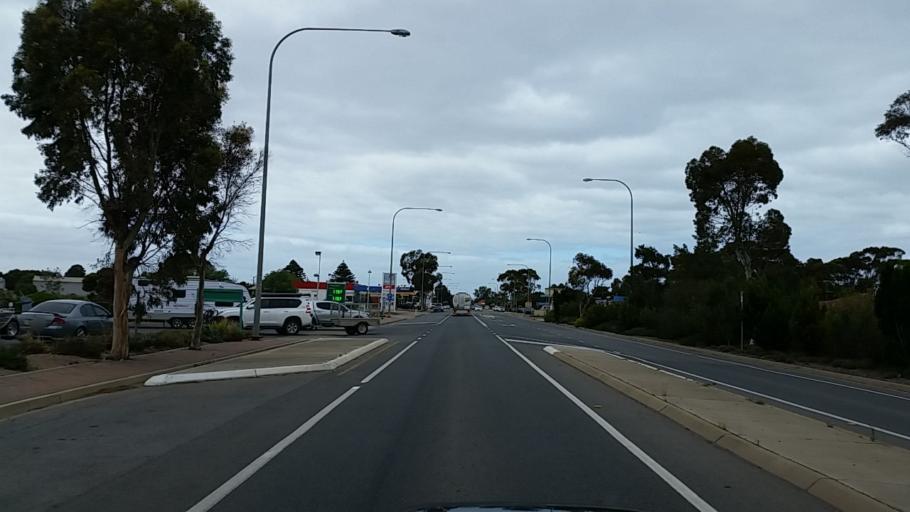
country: AU
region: South Australia
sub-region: Wakefield
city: Balaklava
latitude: -34.1809
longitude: 138.1539
